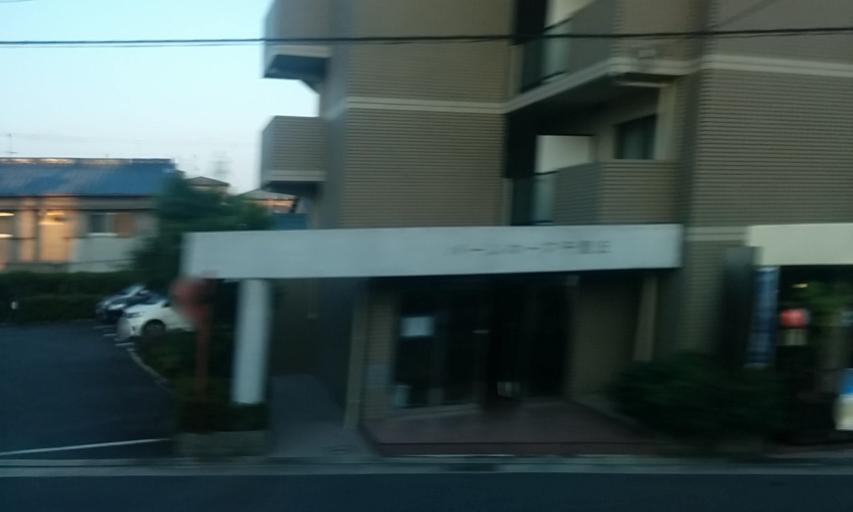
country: JP
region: Osaka
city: Ibaraki
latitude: 34.7932
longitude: 135.5525
